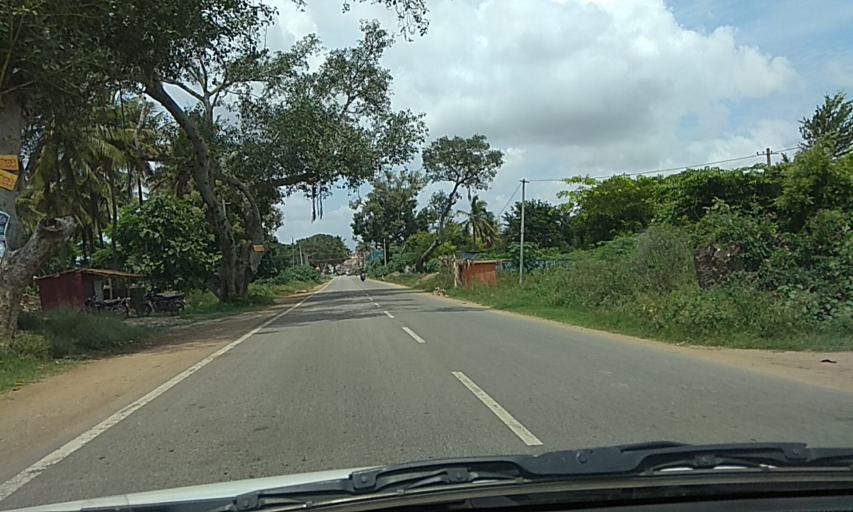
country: IN
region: Karnataka
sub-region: Chamrajnagar
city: Gundlupet
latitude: 11.8098
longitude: 76.6984
